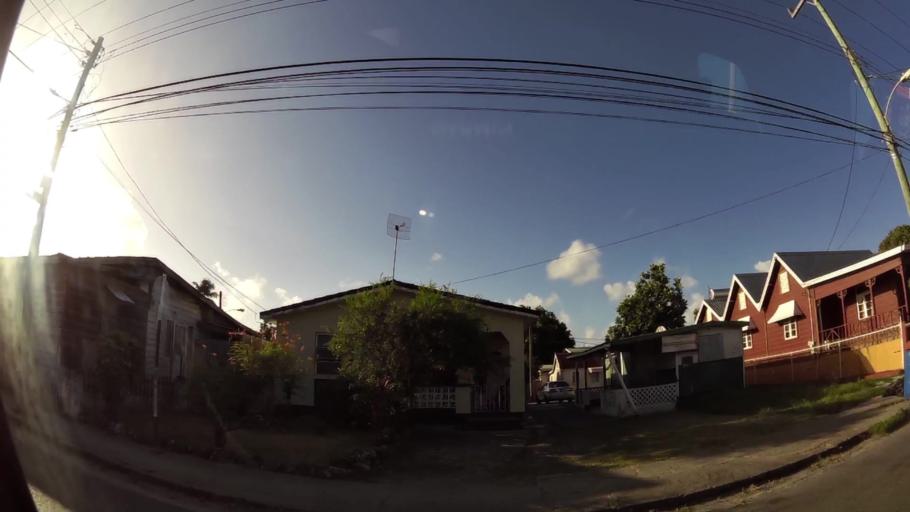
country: BB
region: Saint Michael
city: Bridgetown
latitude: 13.0878
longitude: -59.6054
